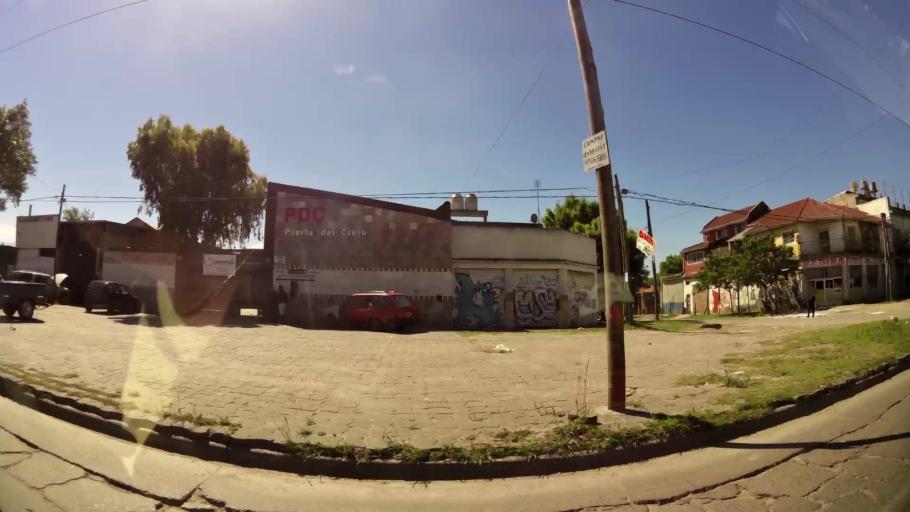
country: AR
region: Buenos Aires
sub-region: Partido de Almirante Brown
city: Adrogue
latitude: -34.7565
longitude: -58.3517
